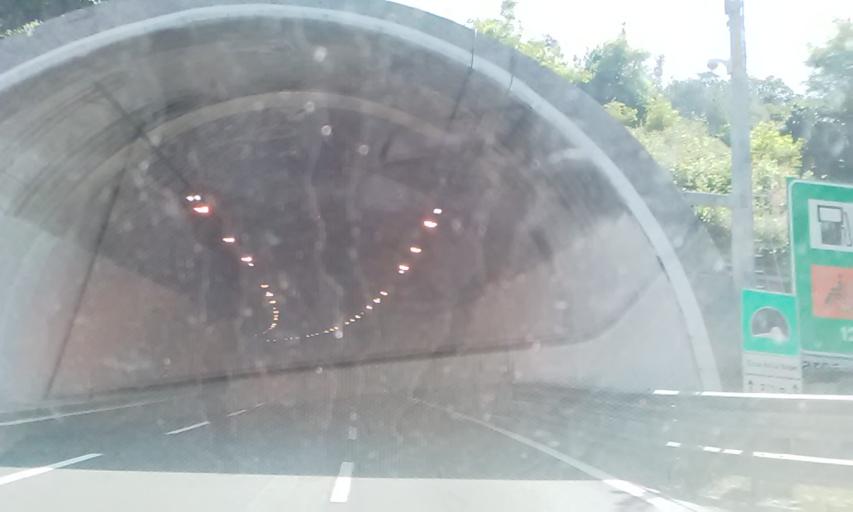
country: IT
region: Liguria
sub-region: Provincia di Genova
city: Mele
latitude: 44.4471
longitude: 8.7341
